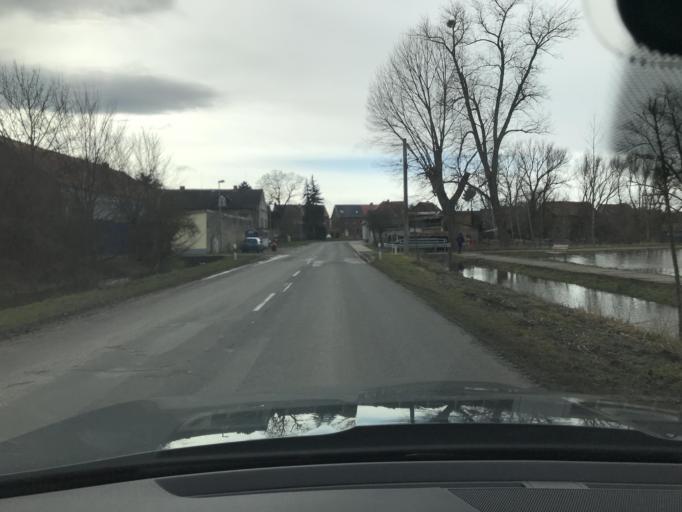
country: DE
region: Saxony-Anhalt
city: Wegeleben
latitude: 51.8868
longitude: 11.1807
